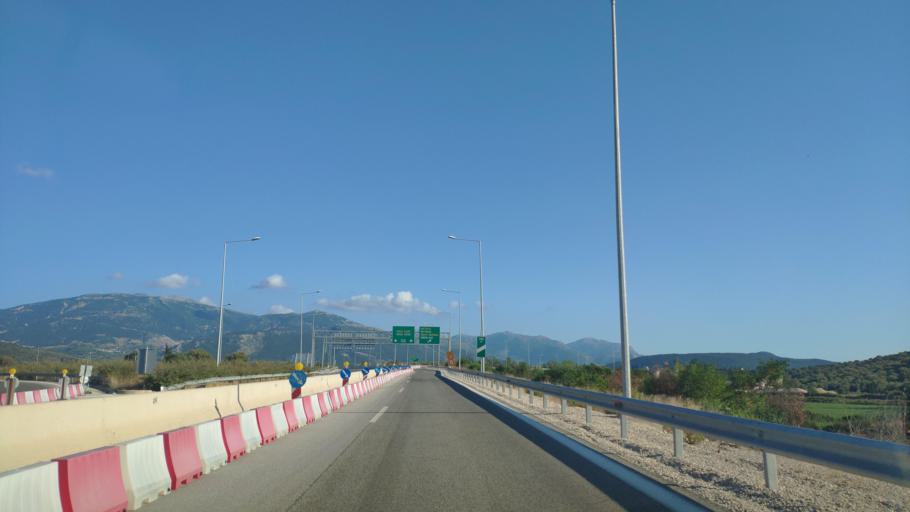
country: GR
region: West Greece
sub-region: Nomos Aitolias kai Akarnanias
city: Vonitsa
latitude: 38.8934
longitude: 20.8977
